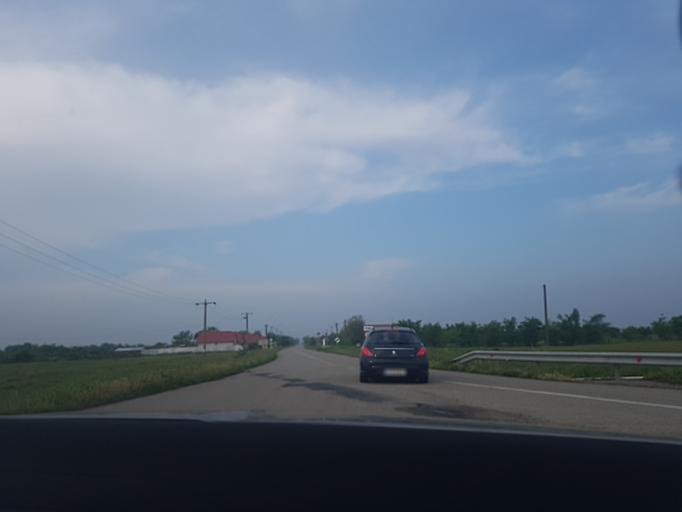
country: RO
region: Timis
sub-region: Comuna Foeni
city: Foeni
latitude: 45.5049
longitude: 20.8797
